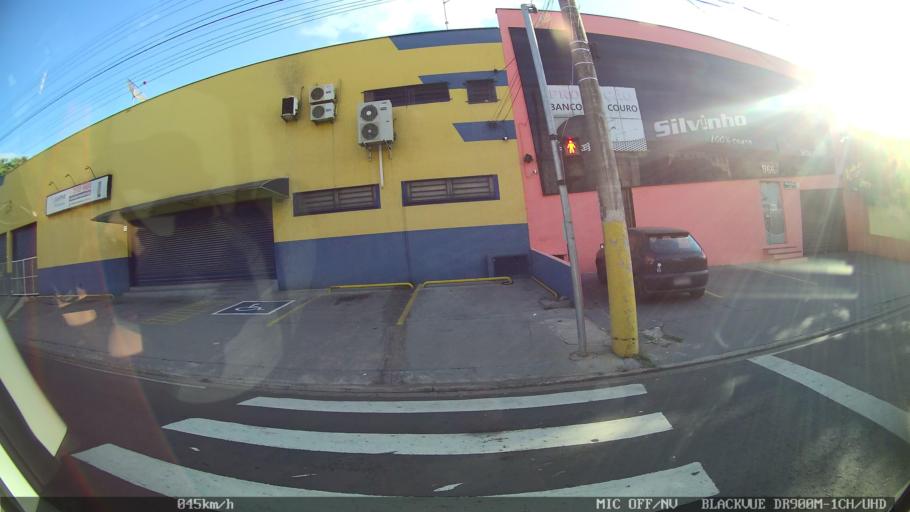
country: BR
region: Sao Paulo
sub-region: Piracicaba
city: Piracicaba
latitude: -22.7437
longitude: -47.6452
